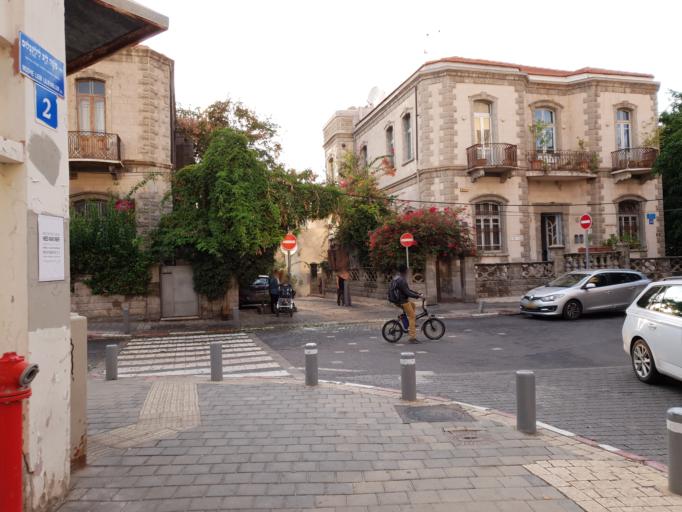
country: IL
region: Tel Aviv
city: Yafo
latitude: 32.0618
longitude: 34.7671
